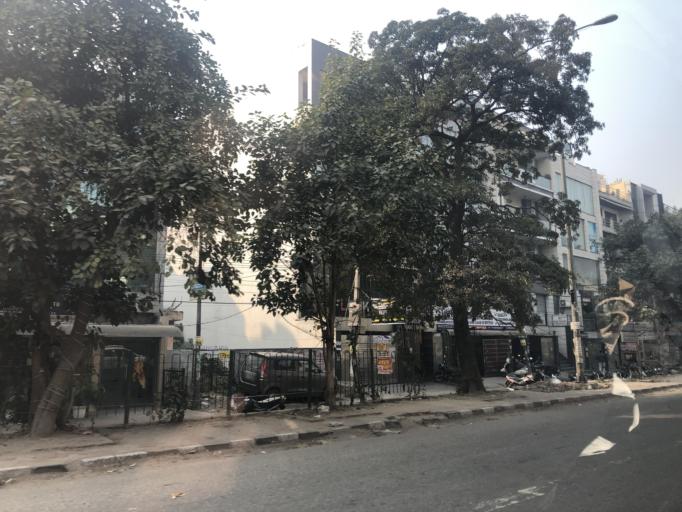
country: IN
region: NCT
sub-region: North West Delhi
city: Pitampura
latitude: 28.6778
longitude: 77.1073
